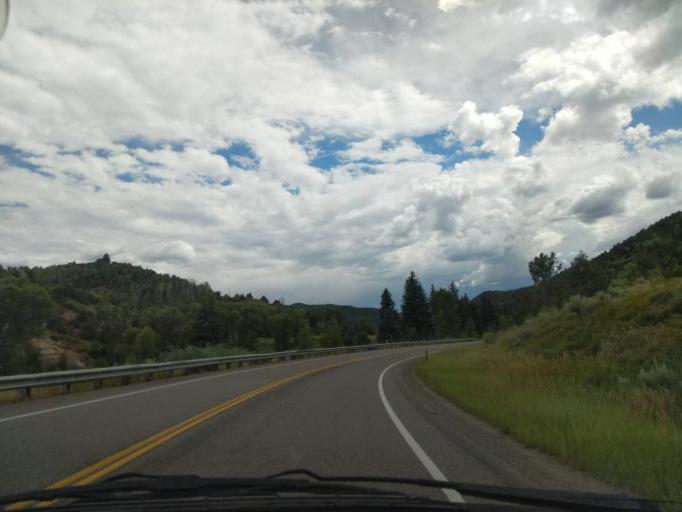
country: US
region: Colorado
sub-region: Delta County
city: Paonia
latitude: 39.0666
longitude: -107.3639
